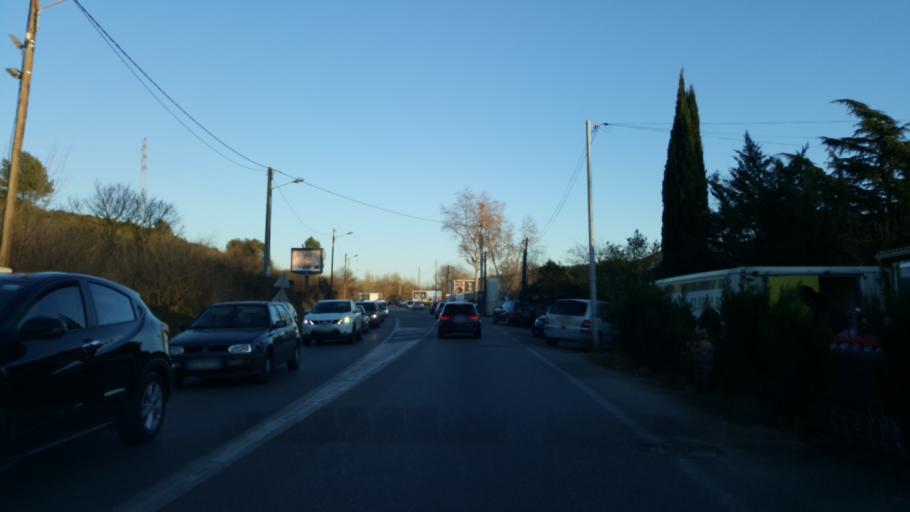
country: FR
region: Provence-Alpes-Cote d'Azur
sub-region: Departement des Bouches-du-Rhone
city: Aix-en-Provence
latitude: 43.5123
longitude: 5.4730
